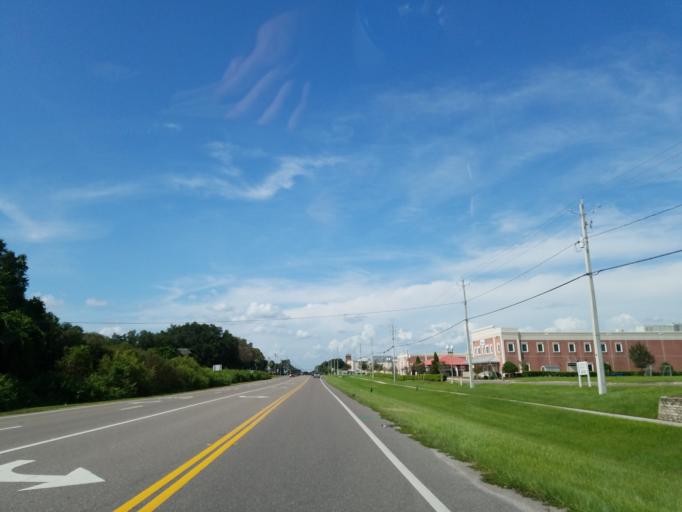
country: US
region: Florida
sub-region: Hillsborough County
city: Riverview
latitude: 27.8883
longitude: -82.3184
